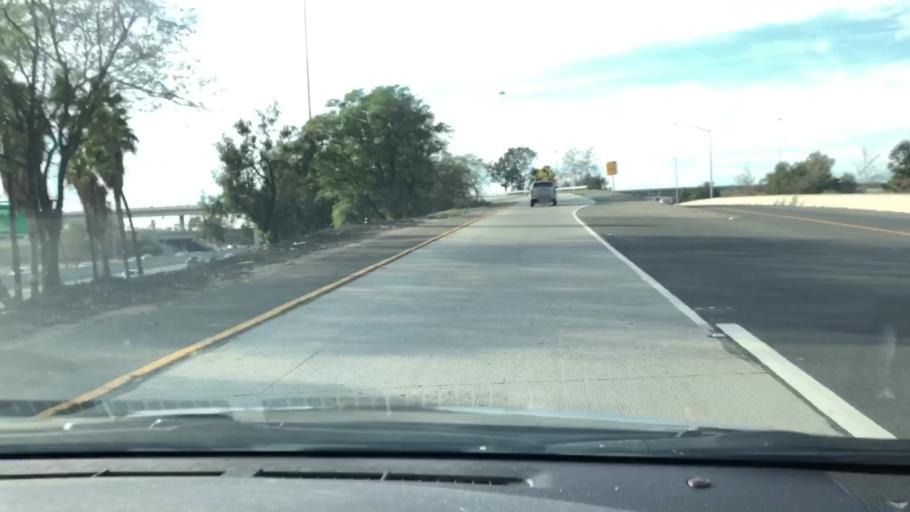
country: US
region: California
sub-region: Orange County
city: Placentia
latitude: 33.8487
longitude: -117.8724
